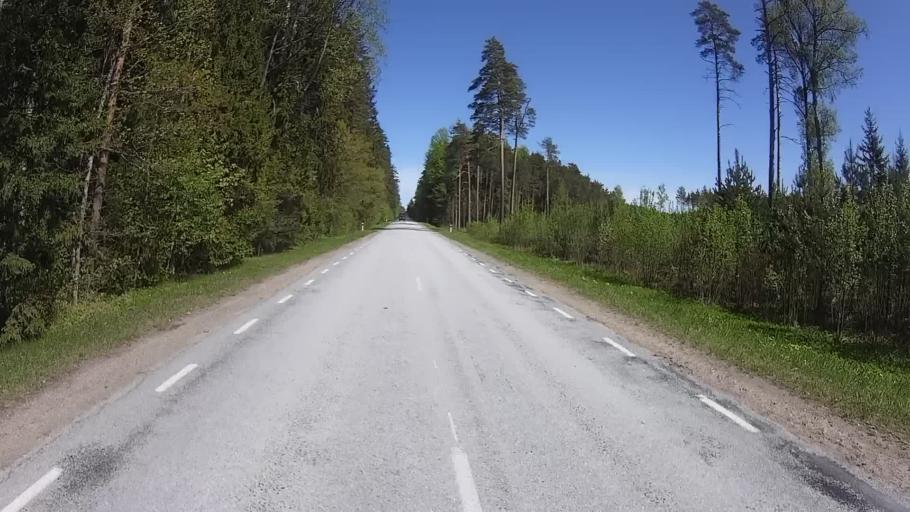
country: EE
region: Polvamaa
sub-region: Raepina vald
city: Rapina
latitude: 58.0789
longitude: 27.4285
